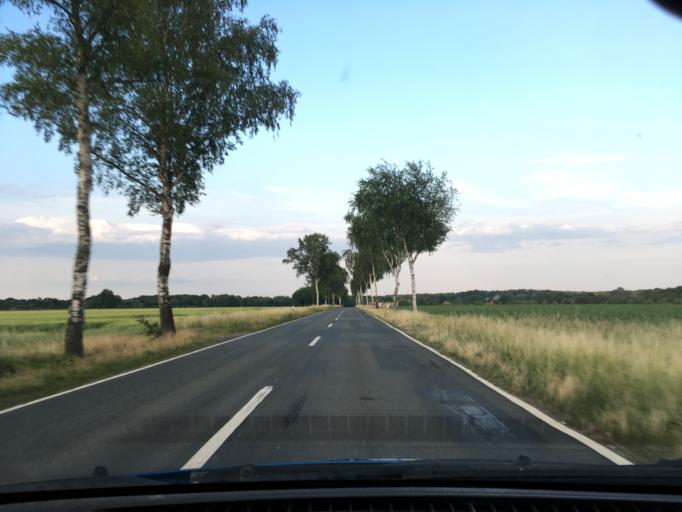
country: DE
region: Lower Saxony
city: Steinhorst
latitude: 52.6898
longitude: 10.3907
